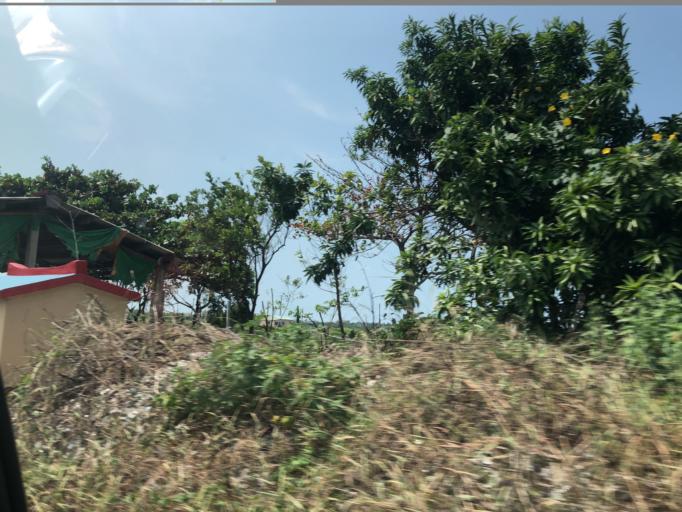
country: TW
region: Taiwan
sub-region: Chiayi
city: Taibao
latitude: 23.4626
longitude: 120.1507
